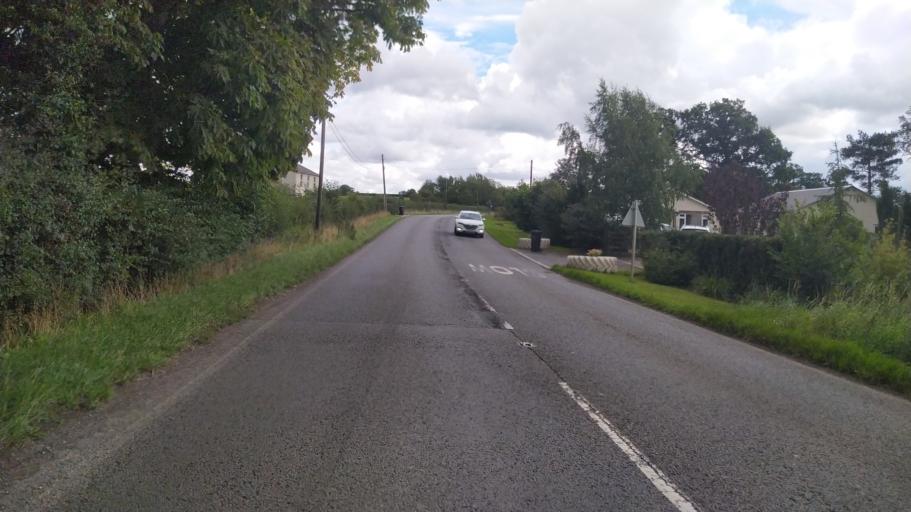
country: GB
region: England
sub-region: Dorset
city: Stalbridge
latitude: 50.9220
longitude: -2.3505
